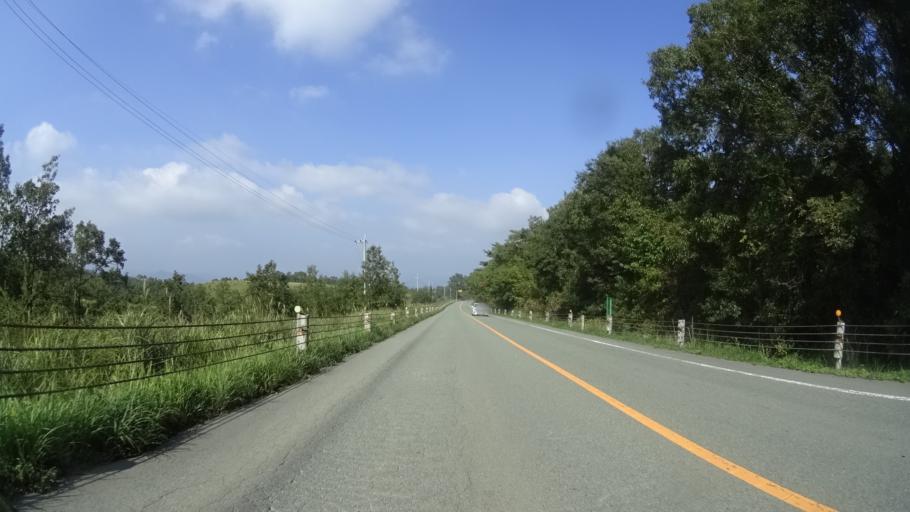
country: JP
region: Kumamoto
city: Aso
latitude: 33.0325
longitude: 131.0646
